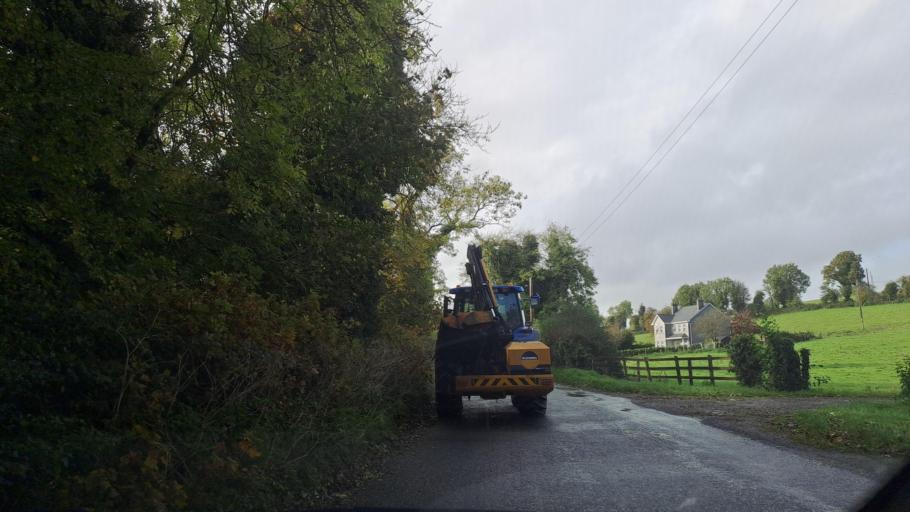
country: IE
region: Ulster
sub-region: County Monaghan
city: Carrickmacross
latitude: 53.8771
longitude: -6.6740
